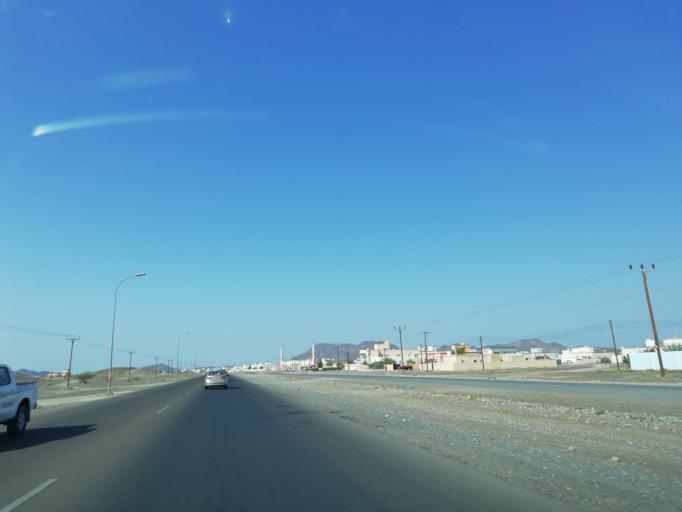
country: OM
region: Ash Sharqiyah
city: Ibra'
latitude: 22.7880
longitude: 58.1461
